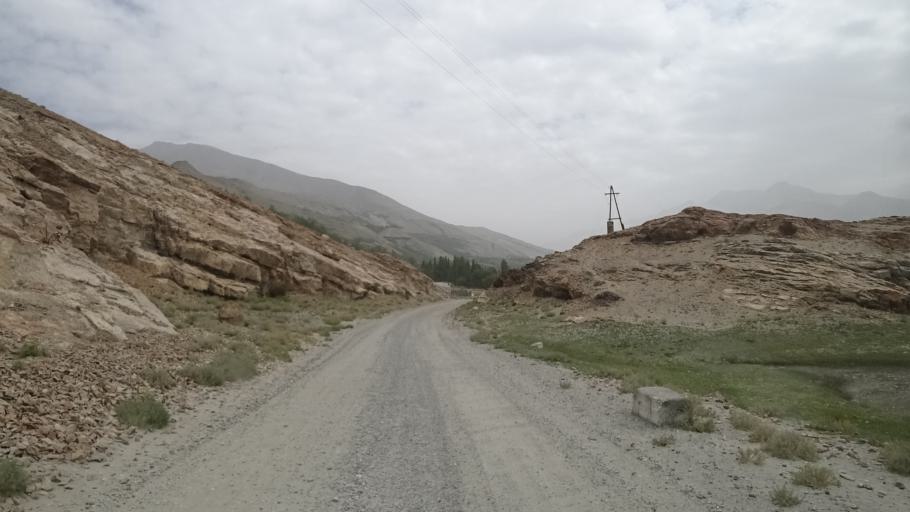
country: AF
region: Badakhshan
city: Khandud
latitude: 37.0265
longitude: 72.6115
